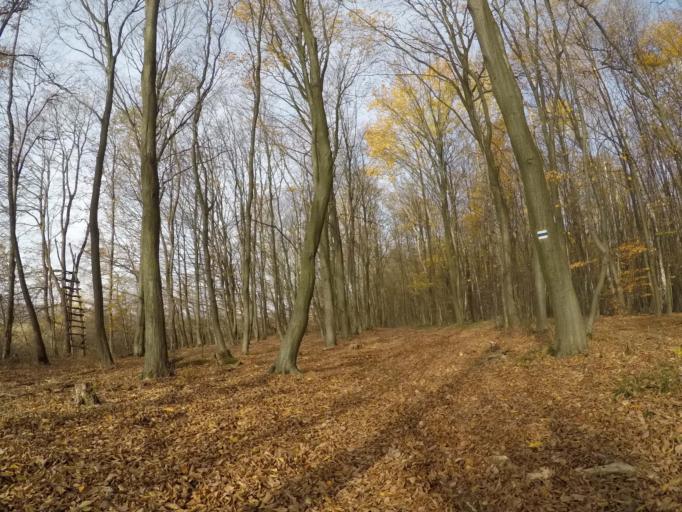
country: SK
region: Presovsky
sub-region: Okres Presov
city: Presov
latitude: 48.9235
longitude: 21.2206
